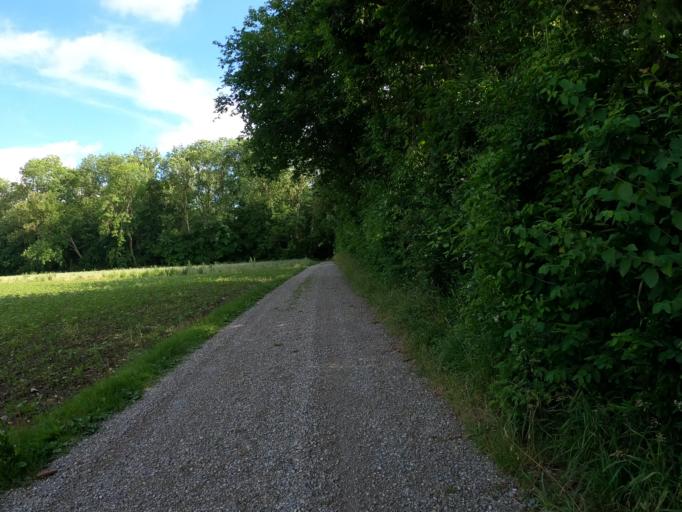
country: DE
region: Bavaria
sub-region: Swabia
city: Nersingen
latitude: 48.4457
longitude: 10.1237
